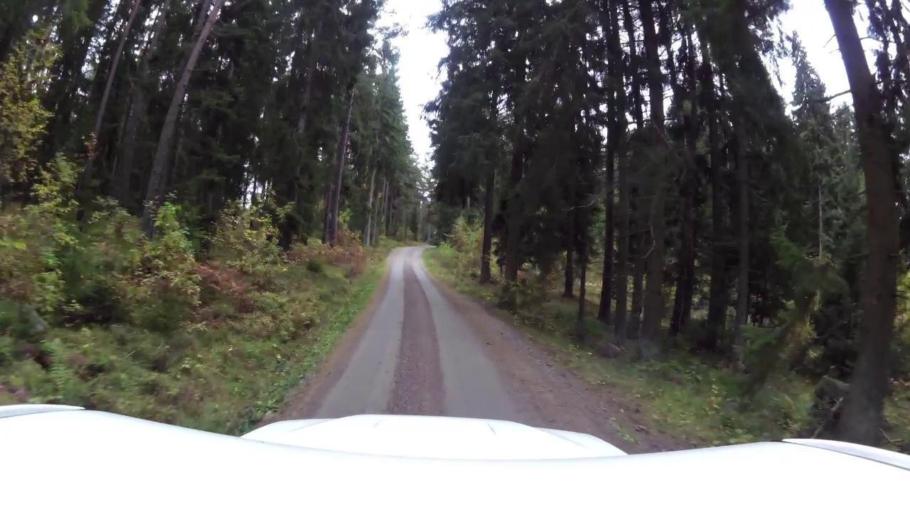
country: SE
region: OEstergoetland
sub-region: Linkopings Kommun
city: Ljungsbro
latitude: 58.5493
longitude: 15.4282
